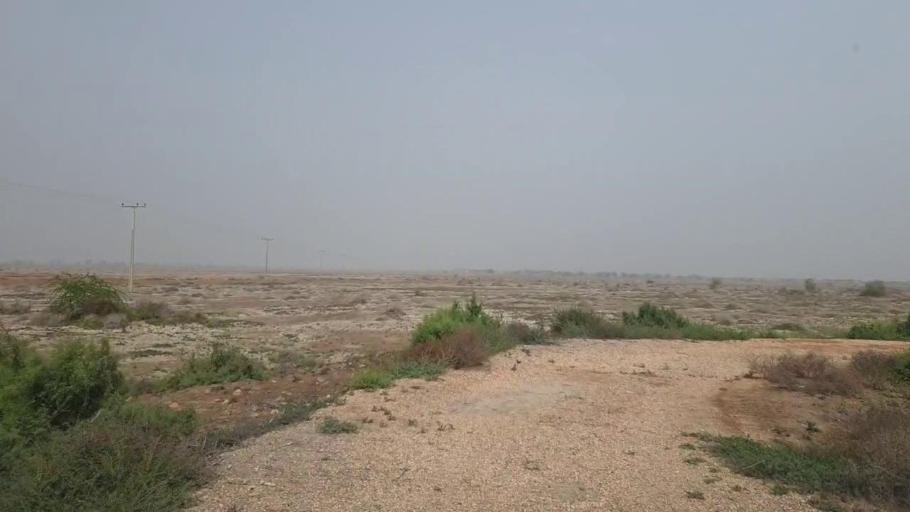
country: PK
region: Sindh
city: Kario
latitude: 24.6675
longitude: 68.6468
